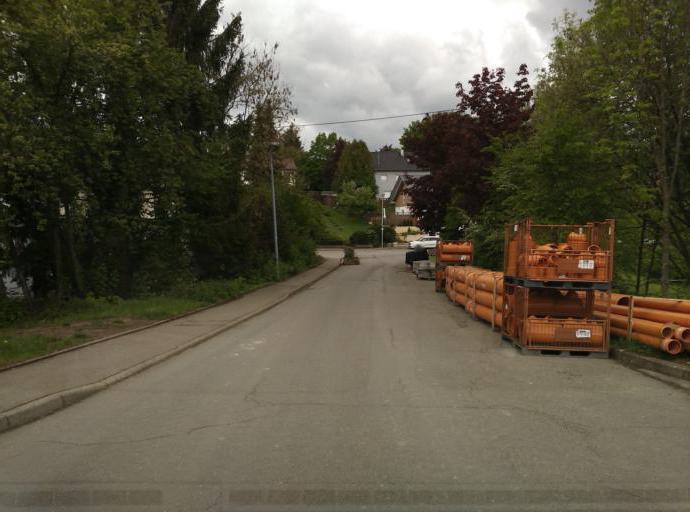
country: DE
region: Baden-Wuerttemberg
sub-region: Tuebingen Region
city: Wannweil
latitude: 48.5143
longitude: 9.1470
